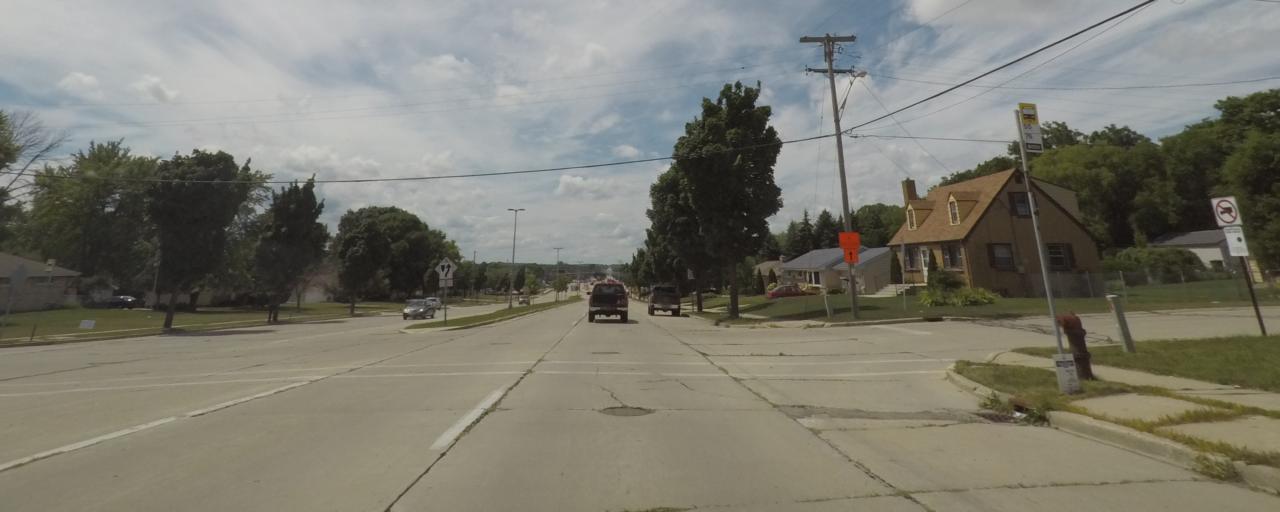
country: US
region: Wisconsin
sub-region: Milwaukee County
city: Greenfield
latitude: 42.9594
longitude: -88.0031
